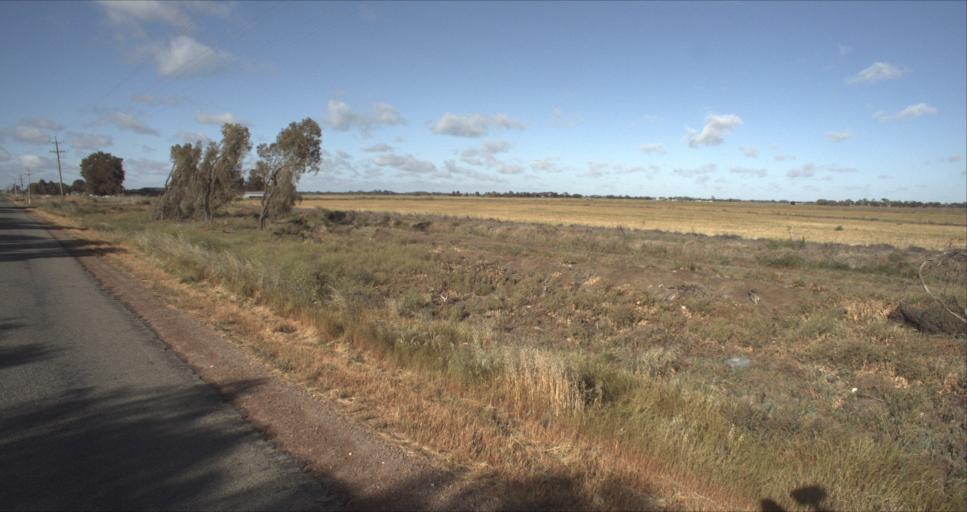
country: AU
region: New South Wales
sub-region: Leeton
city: Leeton
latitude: -34.5154
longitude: 146.3916
